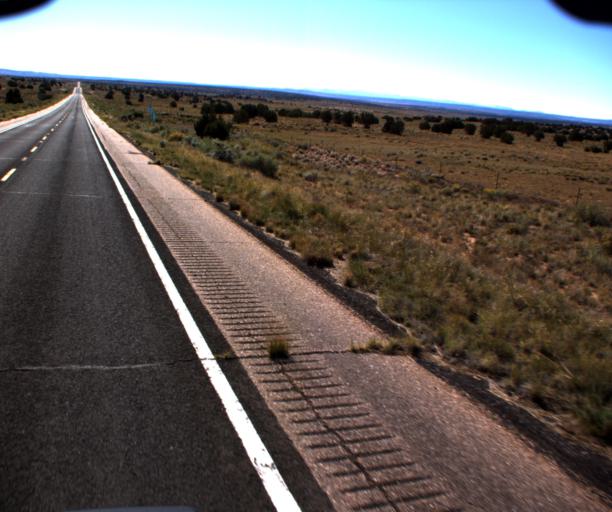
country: US
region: Arizona
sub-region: Navajo County
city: Snowflake
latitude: 34.6843
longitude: -109.7378
